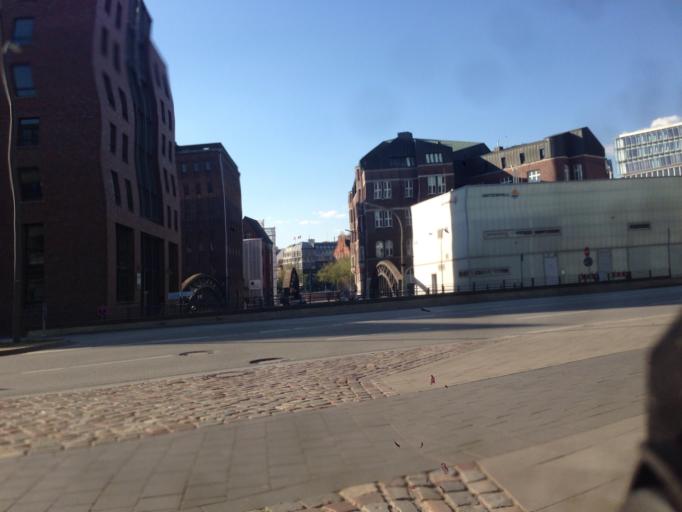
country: DE
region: Hamburg
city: Altstadt
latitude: 53.5455
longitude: 10.0028
